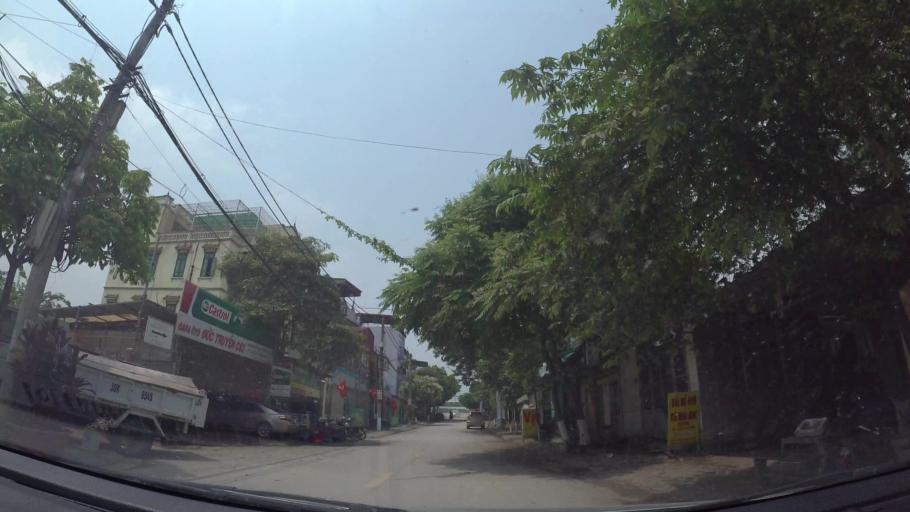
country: VN
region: Ha Noi
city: Tay Ho
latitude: 21.0888
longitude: 105.8087
